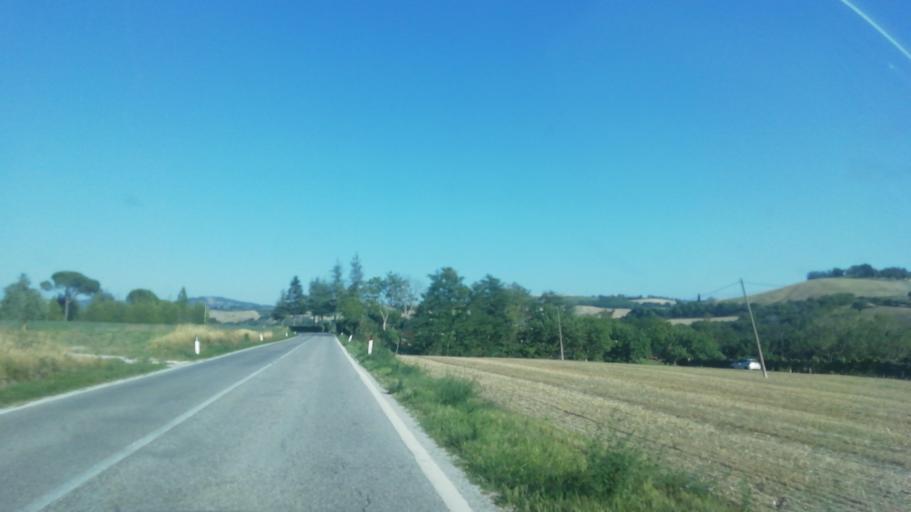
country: IT
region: The Marches
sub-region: Provincia di Pesaro e Urbino
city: Pergola
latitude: 43.5472
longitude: 12.7864
